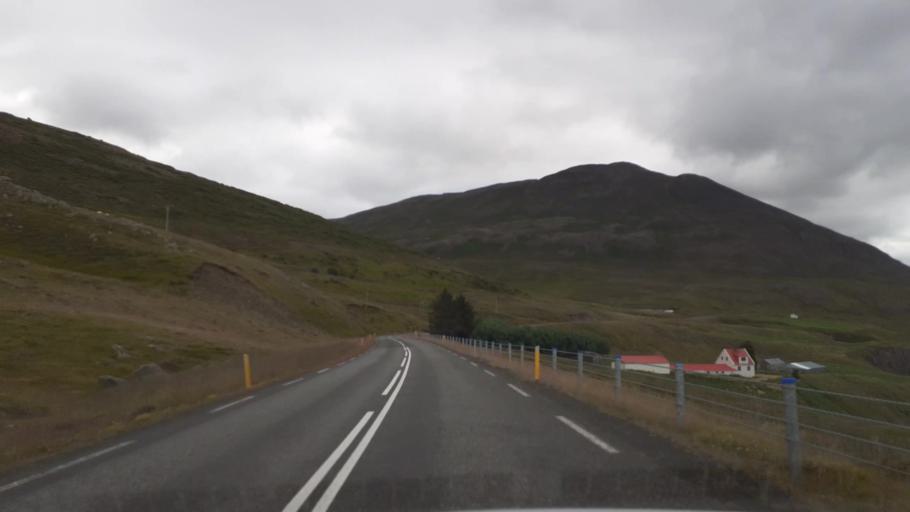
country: IS
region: Northeast
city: Akureyri
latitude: 65.8241
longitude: -18.0543
